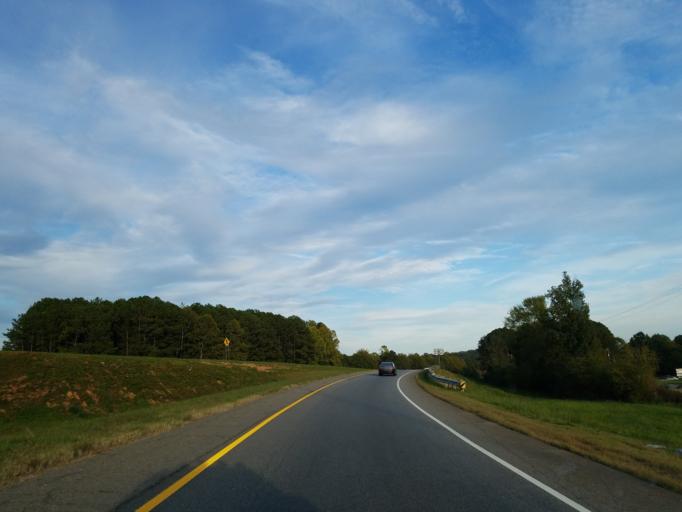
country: US
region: Georgia
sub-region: Bartow County
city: Cartersville
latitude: 34.2205
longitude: -84.8505
